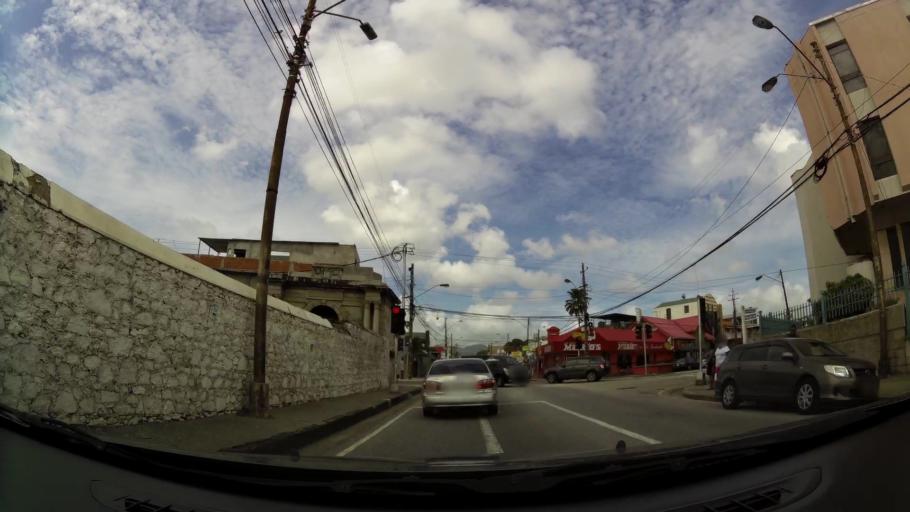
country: TT
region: City of Port of Spain
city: Port-of-Spain
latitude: 10.6603
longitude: -61.5166
